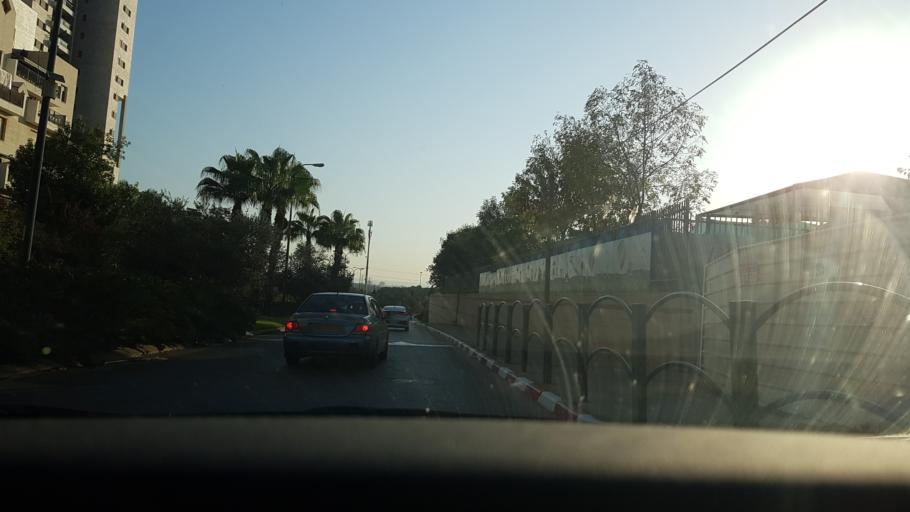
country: IL
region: Central District
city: Ness Ziona
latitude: 31.9057
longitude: 34.8224
